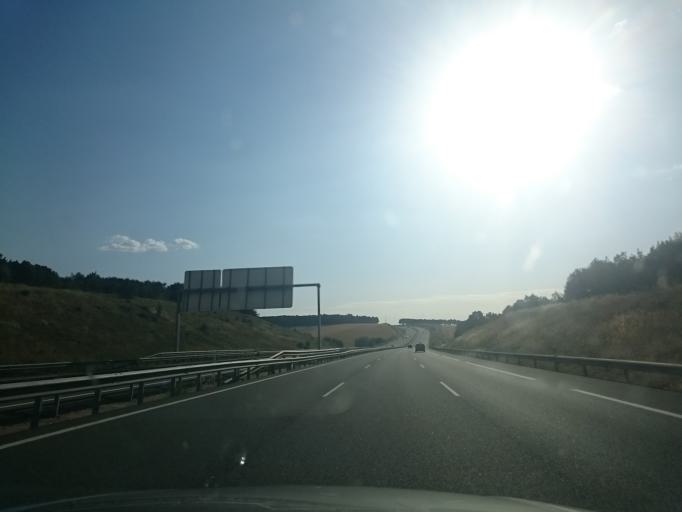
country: ES
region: Castille and Leon
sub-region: Provincia de Burgos
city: Cardenajimeno
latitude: 42.3309
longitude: -3.6373
